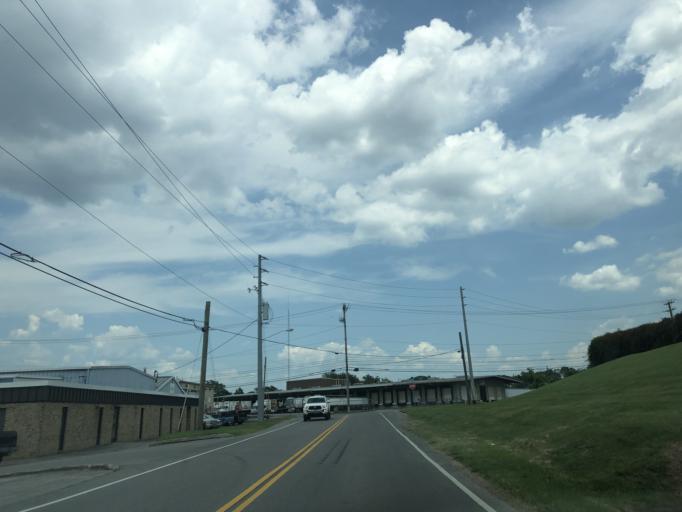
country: US
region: Tennessee
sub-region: Davidson County
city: Nashville
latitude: 36.1371
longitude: -86.7479
